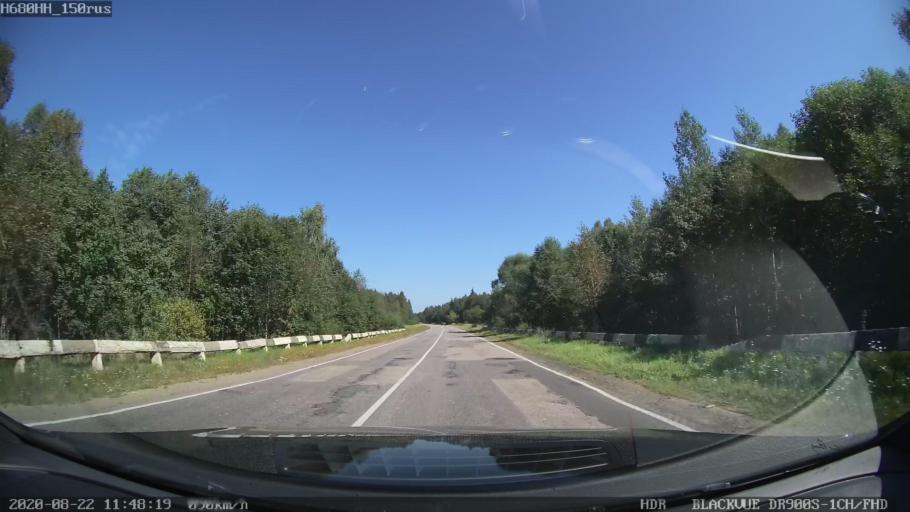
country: RU
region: Tverskaya
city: Sakharovo
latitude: 57.0615
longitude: 36.1013
